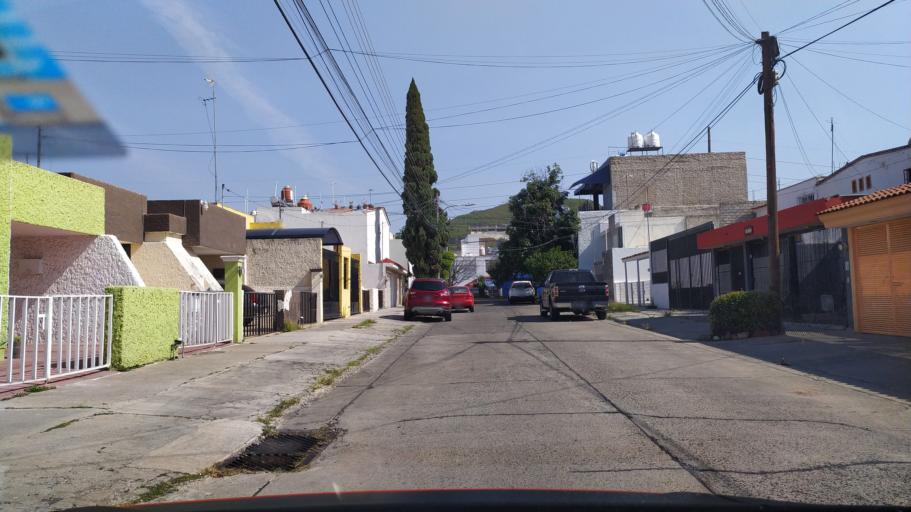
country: MX
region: Jalisco
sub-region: Tlajomulco de Zuniga
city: La Tijera
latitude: 20.6224
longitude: -103.4168
